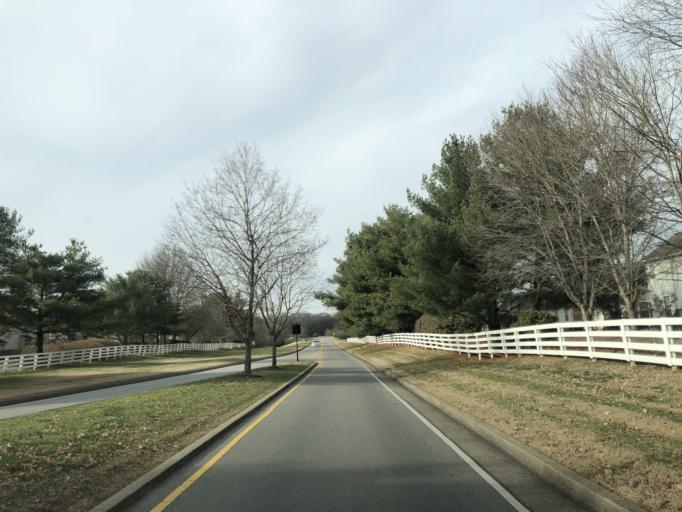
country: US
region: Tennessee
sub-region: Williamson County
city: Franklin
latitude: 35.9659
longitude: -86.8945
